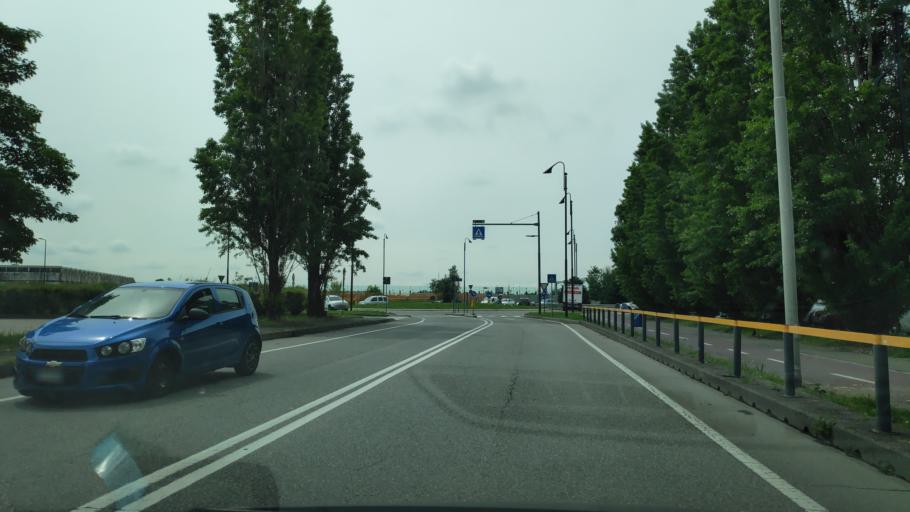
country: IT
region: Lombardy
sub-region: Citta metropolitana di Milano
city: Segrate
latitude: 45.4864
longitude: 9.2890
